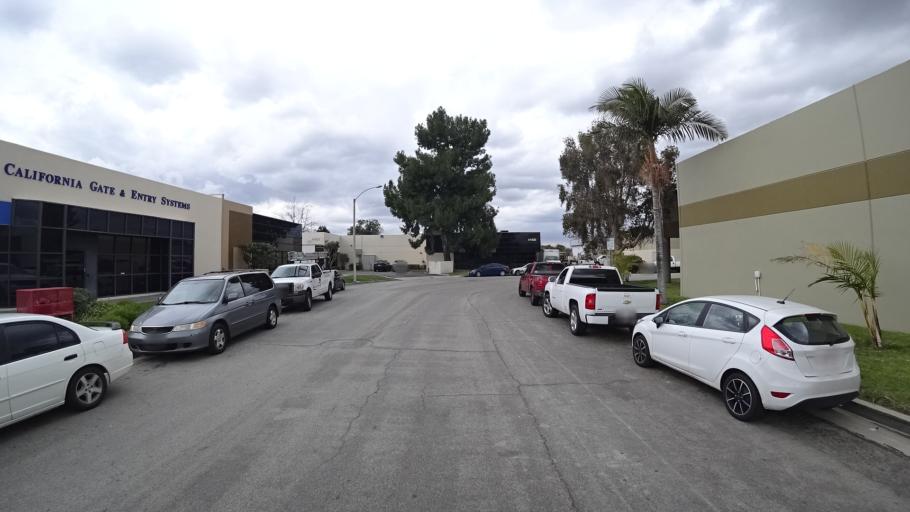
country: US
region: California
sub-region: Orange County
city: Placentia
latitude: 33.8618
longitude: -117.8649
